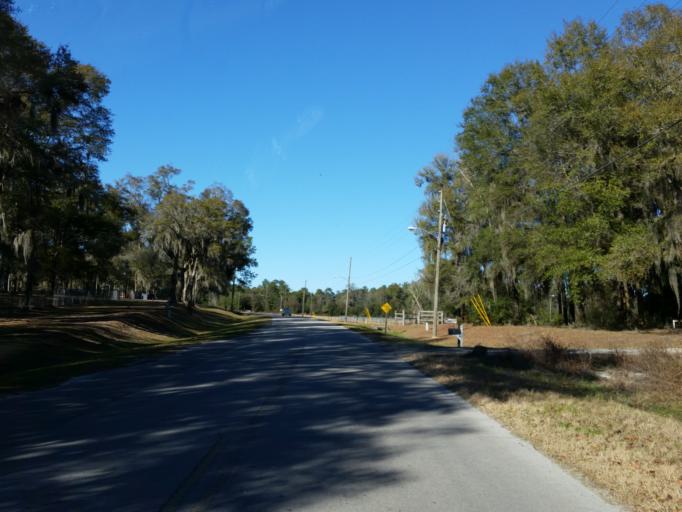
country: US
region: Florida
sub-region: Hamilton County
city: Jasper
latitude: 30.5055
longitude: -82.9529
